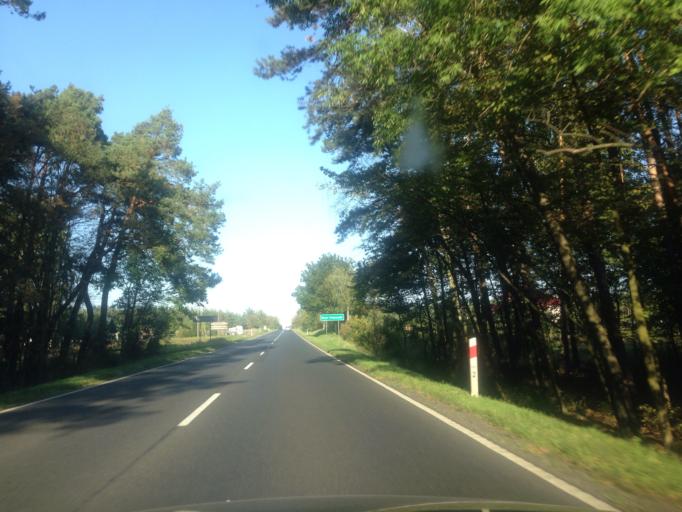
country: PL
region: Kujawsko-Pomorskie
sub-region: Powiat brodnicki
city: Brzozie
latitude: 53.3147
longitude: 19.5238
